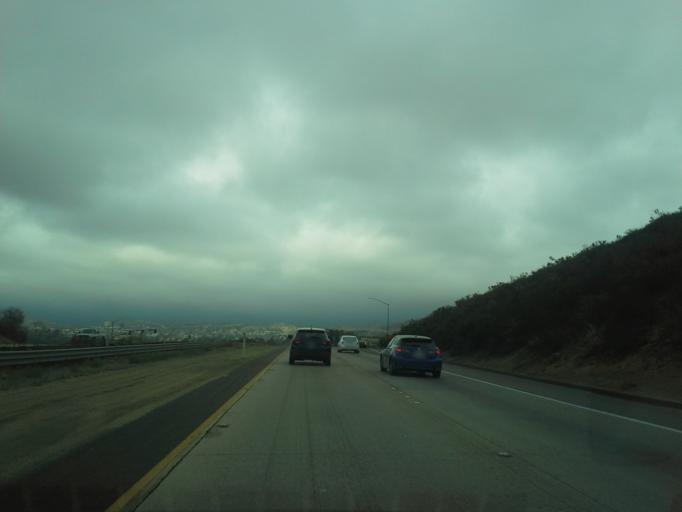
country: US
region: California
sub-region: San Diego County
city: Granite Hills
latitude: 32.8241
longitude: -116.9065
